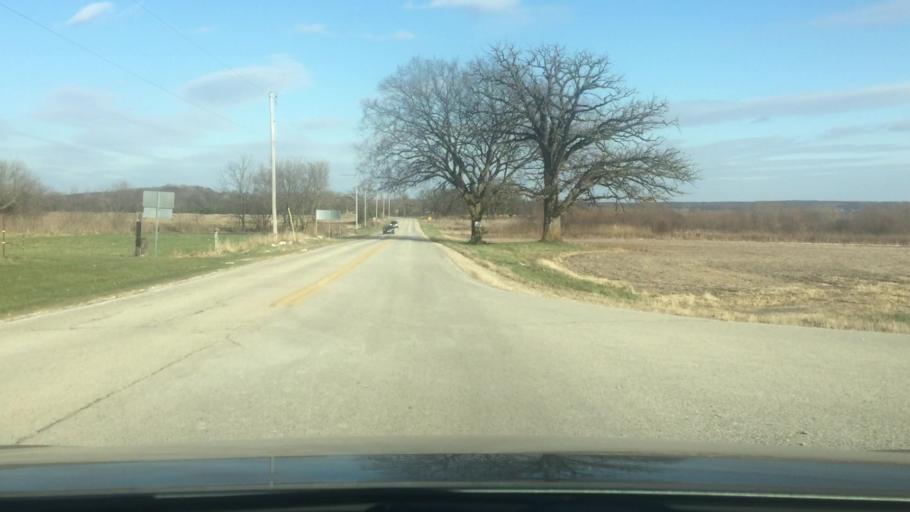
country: US
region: Wisconsin
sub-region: Waukesha County
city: Eagle
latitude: 42.9174
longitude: -88.5198
